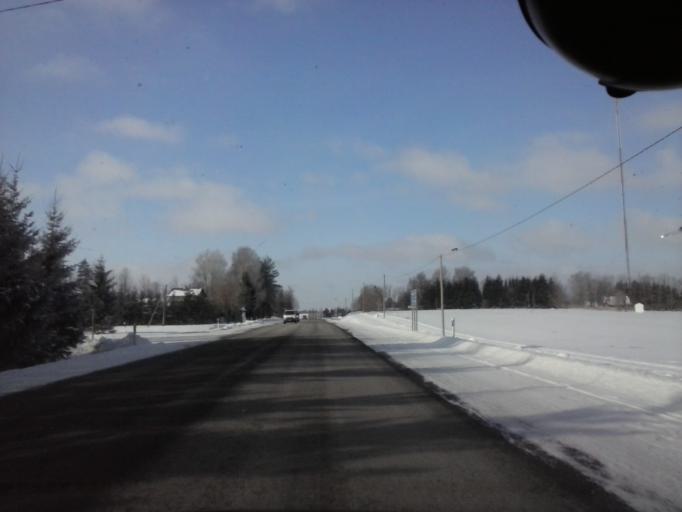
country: EE
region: Tartu
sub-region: Puhja vald
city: Puhja
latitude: 58.3431
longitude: 26.3522
